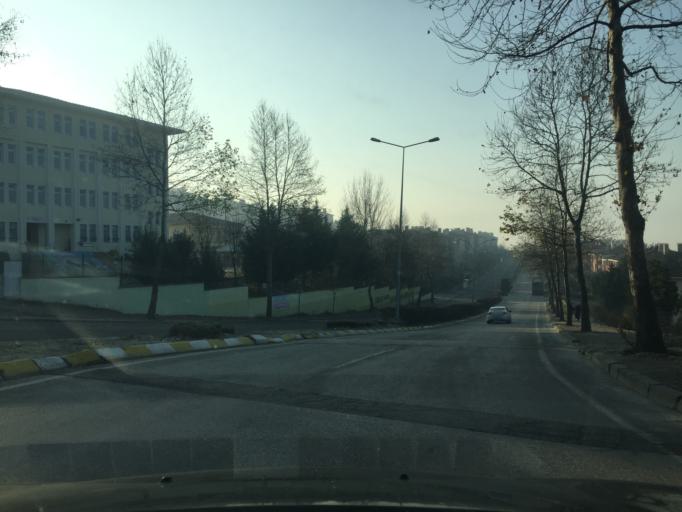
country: TR
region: Duzce
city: Duzce
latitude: 40.8667
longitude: 31.2307
